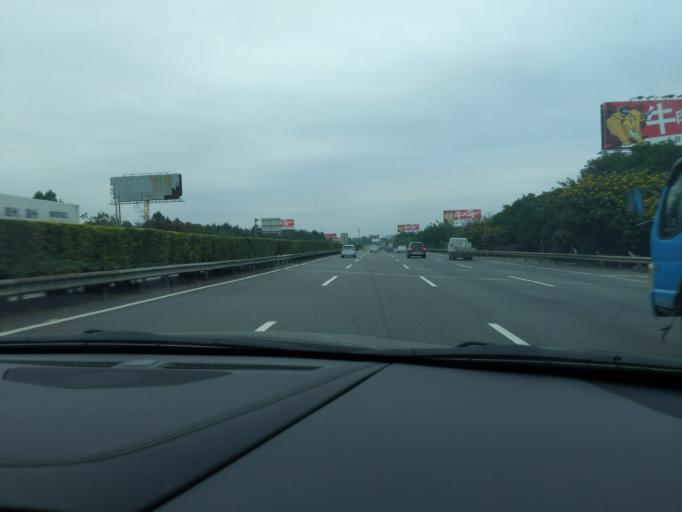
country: CN
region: Fujian
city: Neikeng
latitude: 24.7635
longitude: 118.4493
